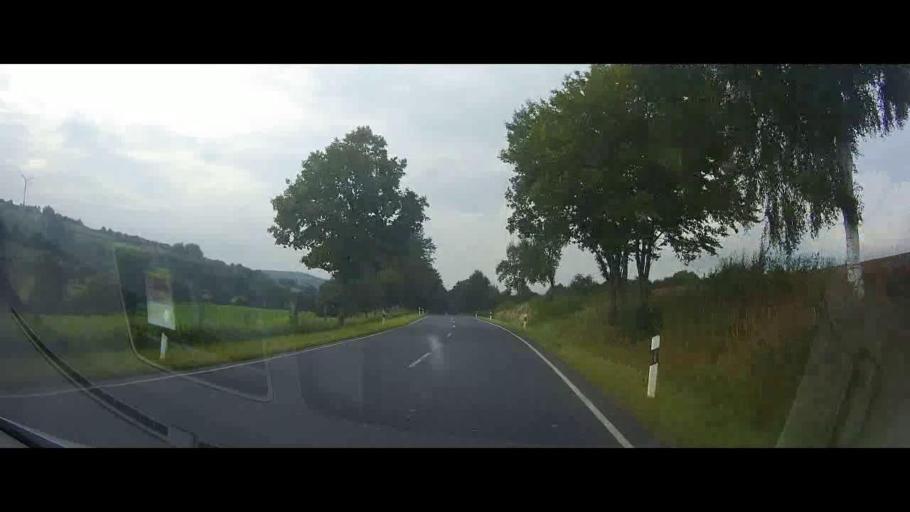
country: DE
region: Lower Saxony
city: Adelebsen
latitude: 51.5743
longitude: 9.7057
